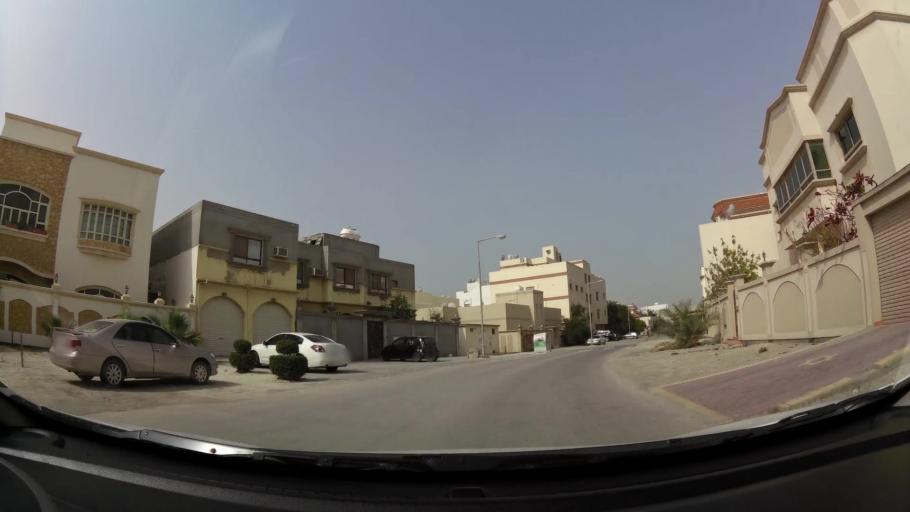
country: BH
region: Manama
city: Jidd Hafs
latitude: 26.2338
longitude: 50.5274
